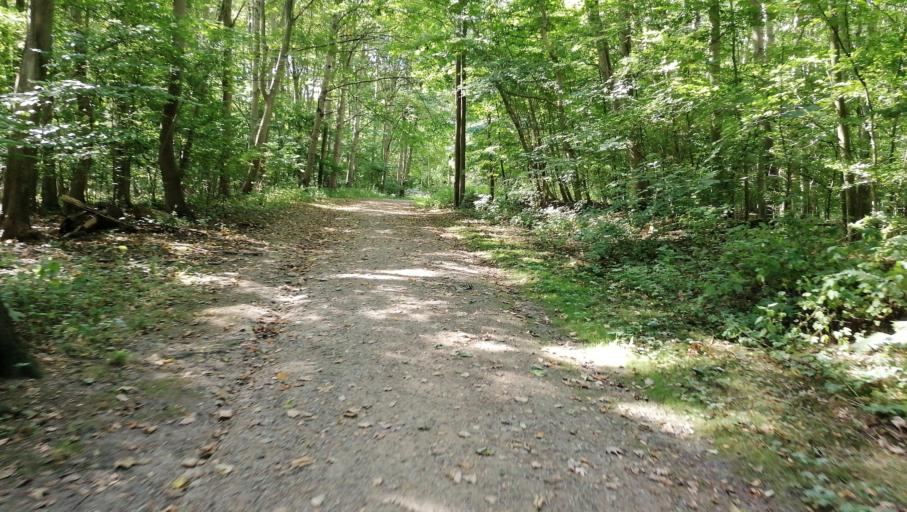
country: DK
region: Zealand
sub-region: Holbaek Kommune
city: Holbaek
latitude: 55.7119
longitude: 11.6899
